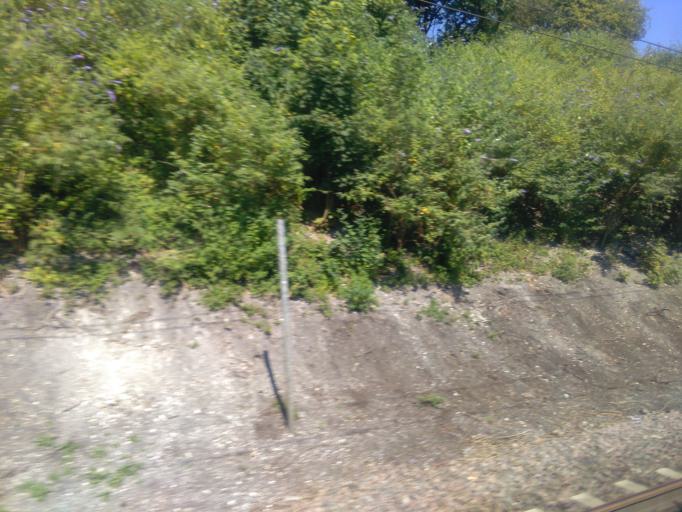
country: GB
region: England
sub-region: Luton
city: Luton
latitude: 51.8705
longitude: -0.3921
